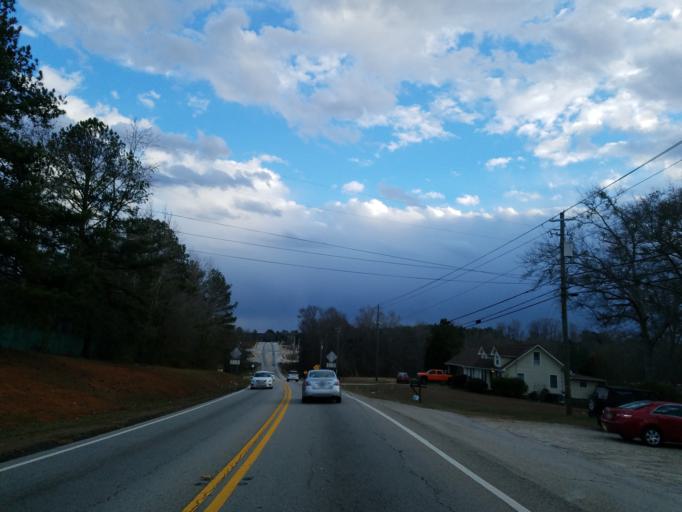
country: US
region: Georgia
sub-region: Henry County
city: McDonough
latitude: 33.4731
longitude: -84.1624
